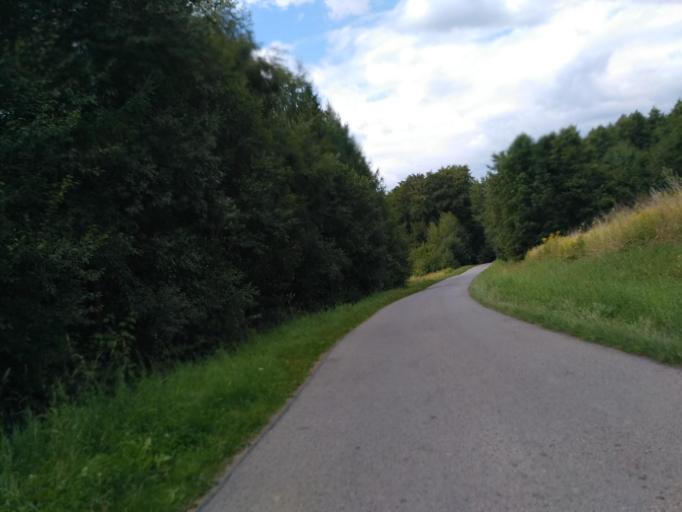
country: PL
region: Subcarpathian Voivodeship
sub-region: Powiat rzeszowski
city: Chmielnik
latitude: 49.9521
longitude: 22.1330
